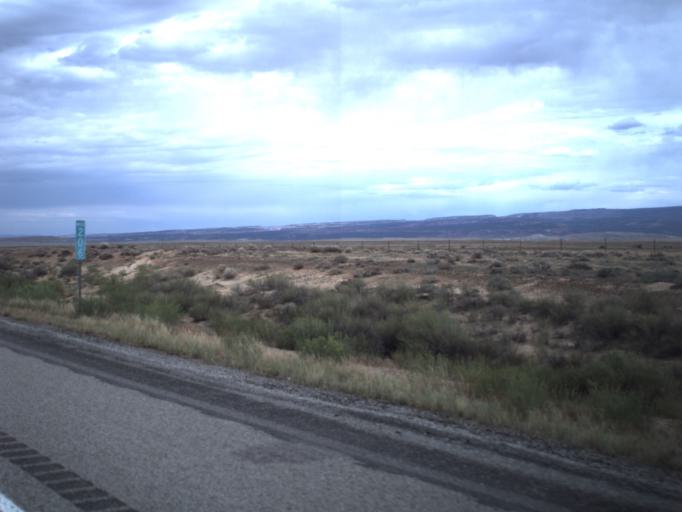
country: US
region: Utah
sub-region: Grand County
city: Moab
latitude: 38.9510
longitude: -109.3915
